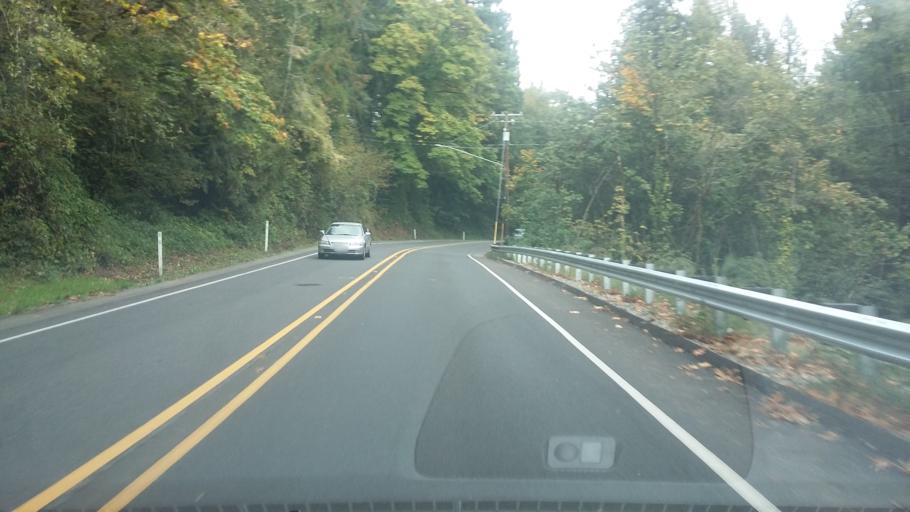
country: US
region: Washington
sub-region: Clark County
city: Ridgefield
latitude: 45.8155
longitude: -122.7231
